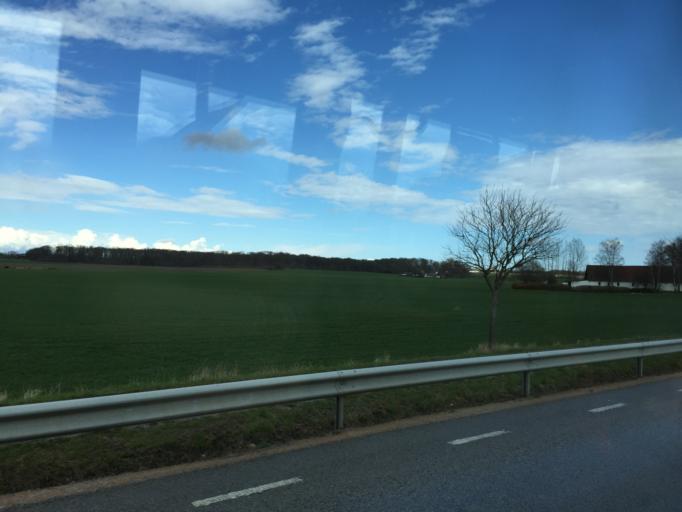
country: SE
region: Skane
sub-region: Lunds Kommun
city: Genarp
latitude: 55.6703
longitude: 13.3118
